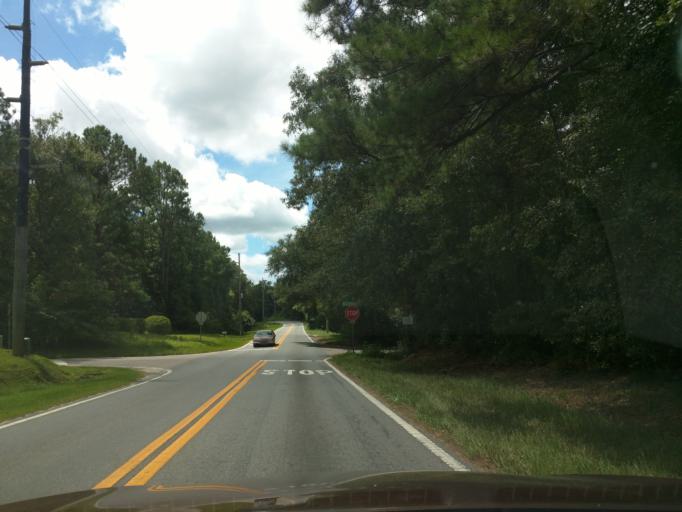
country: US
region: Florida
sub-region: Leon County
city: Tallahassee
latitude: 30.5179
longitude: -84.1299
